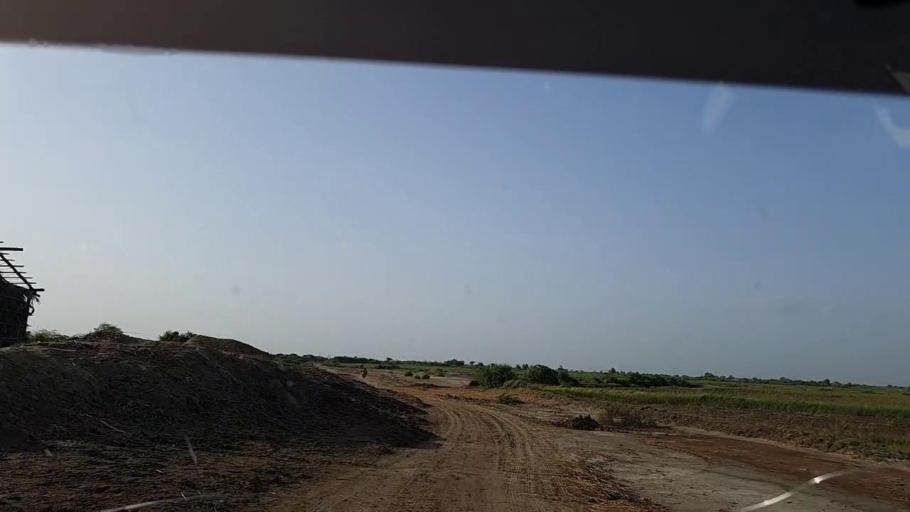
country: PK
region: Sindh
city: Badin
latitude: 24.5708
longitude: 68.8778
